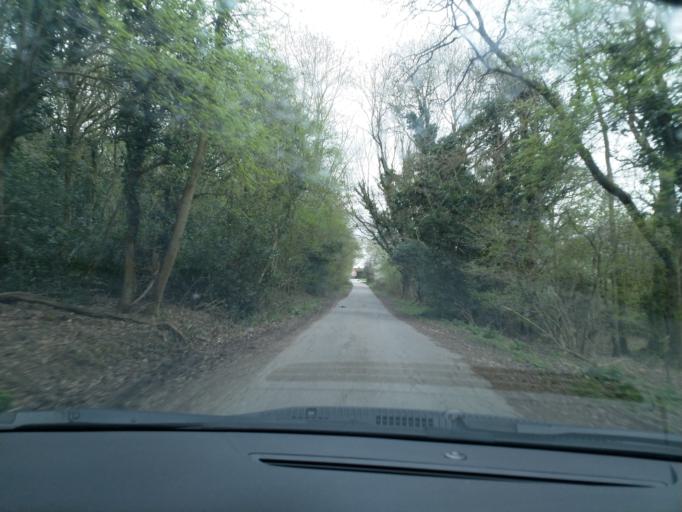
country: GB
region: England
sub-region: Warwickshire
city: Henley in Arden
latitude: 52.2920
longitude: -1.7261
